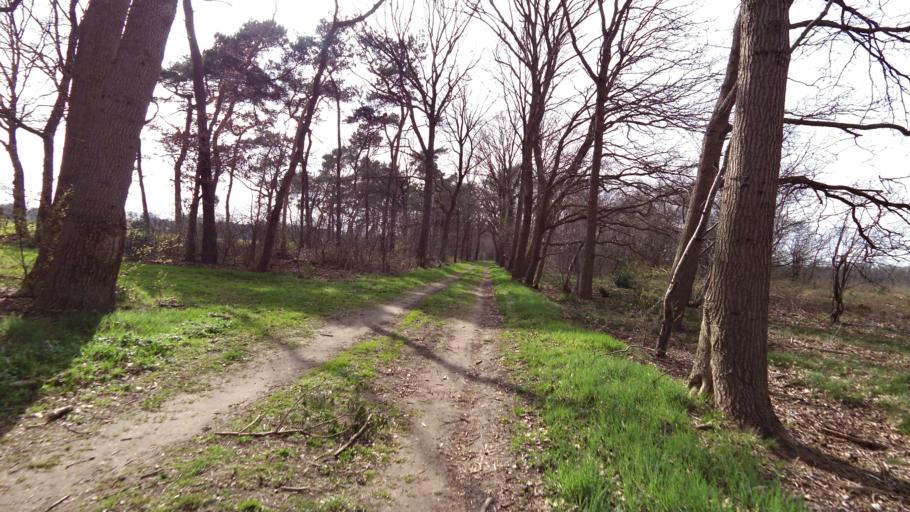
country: NL
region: Gelderland
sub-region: Gemeente Barneveld
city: Voorthuizen
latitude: 52.2065
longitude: 5.6026
